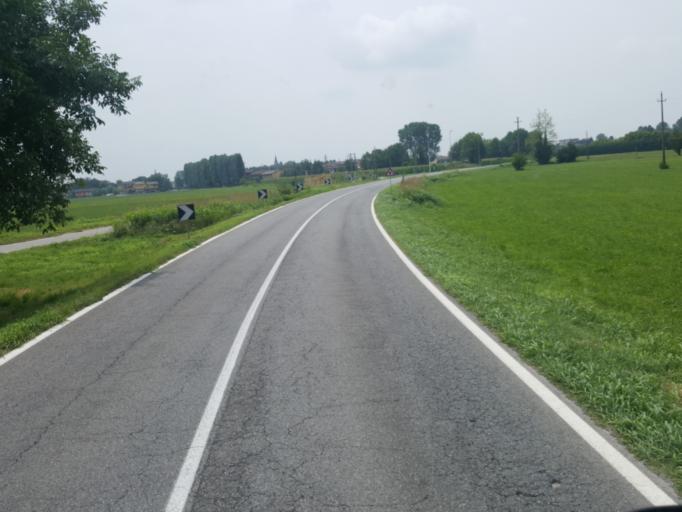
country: IT
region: Lombardy
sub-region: Provincia di Cremona
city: Agnadello
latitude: 45.4543
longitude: 9.5579
